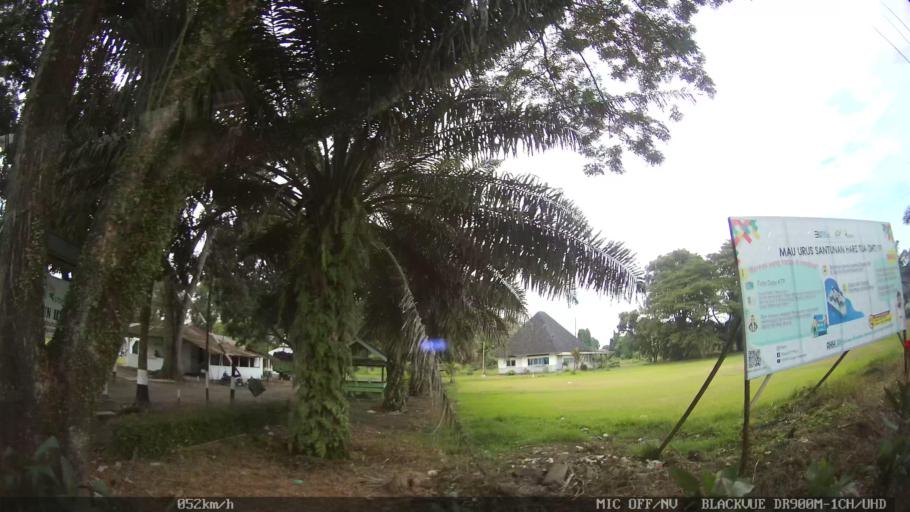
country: ID
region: North Sumatra
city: Sunggal
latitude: 3.6350
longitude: 98.5929
